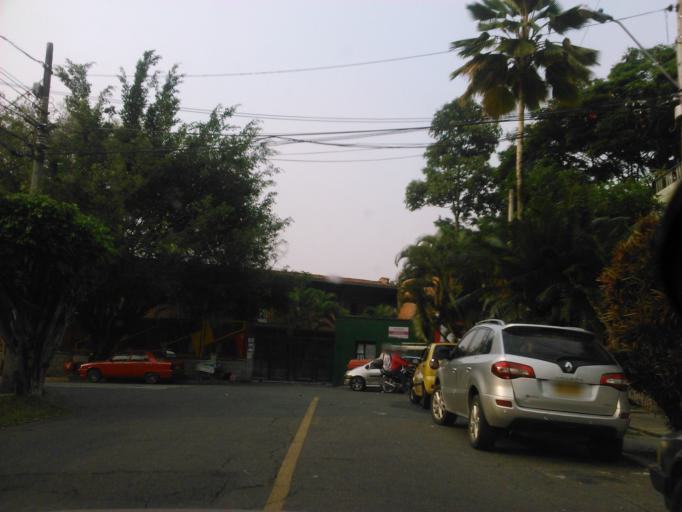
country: CO
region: Antioquia
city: Medellin
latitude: 6.2561
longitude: -75.5993
